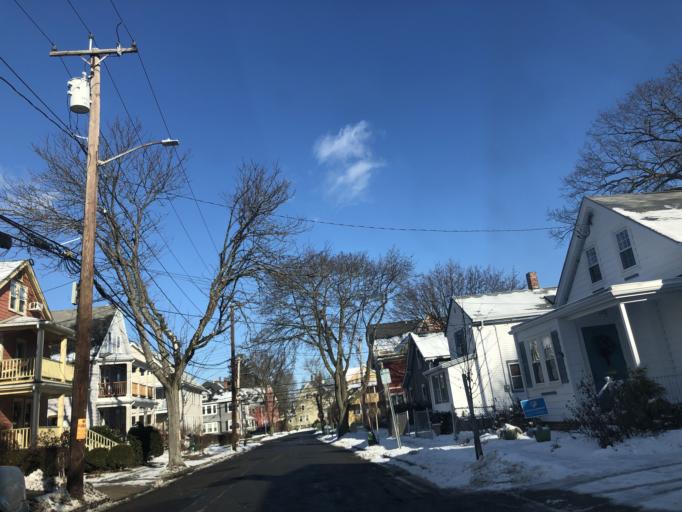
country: US
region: Massachusetts
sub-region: Middlesex County
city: Arlington
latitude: 42.4149
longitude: -71.1481
